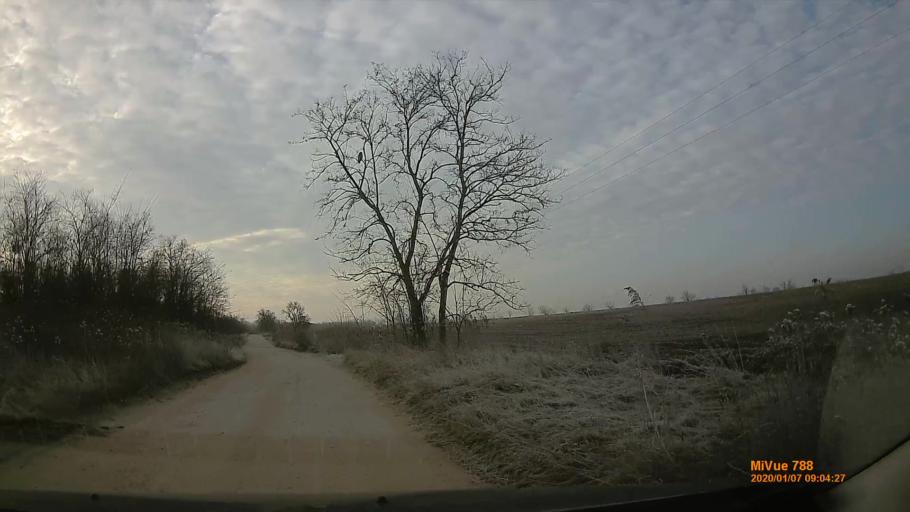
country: HU
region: Gyor-Moson-Sopron
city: Rajka
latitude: 47.9848
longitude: 17.1897
